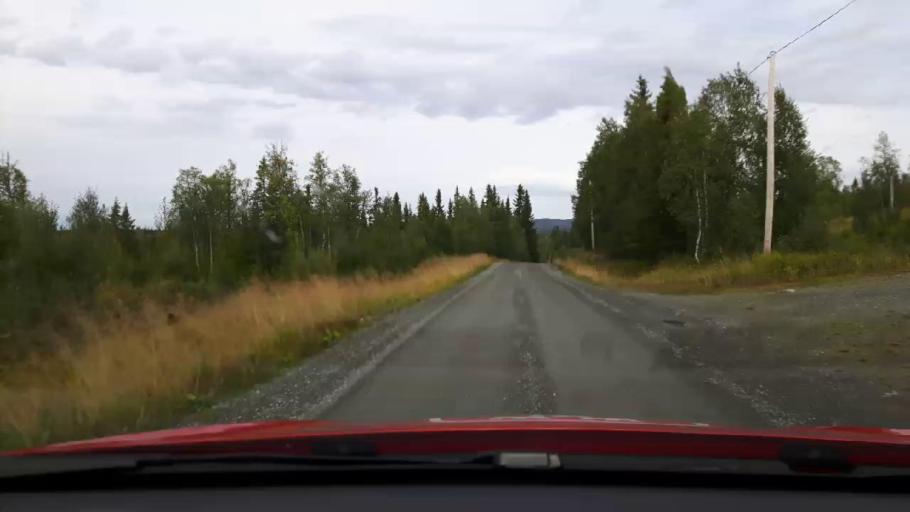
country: SE
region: Jaemtland
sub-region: Are Kommun
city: Are
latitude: 63.7626
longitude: 13.0915
